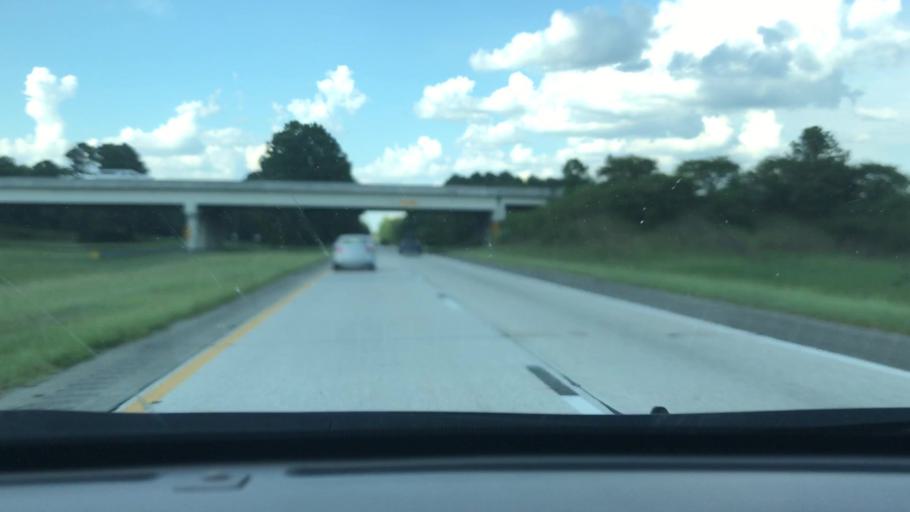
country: US
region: South Carolina
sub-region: Florence County
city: Timmonsville
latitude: 34.1108
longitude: -79.9114
